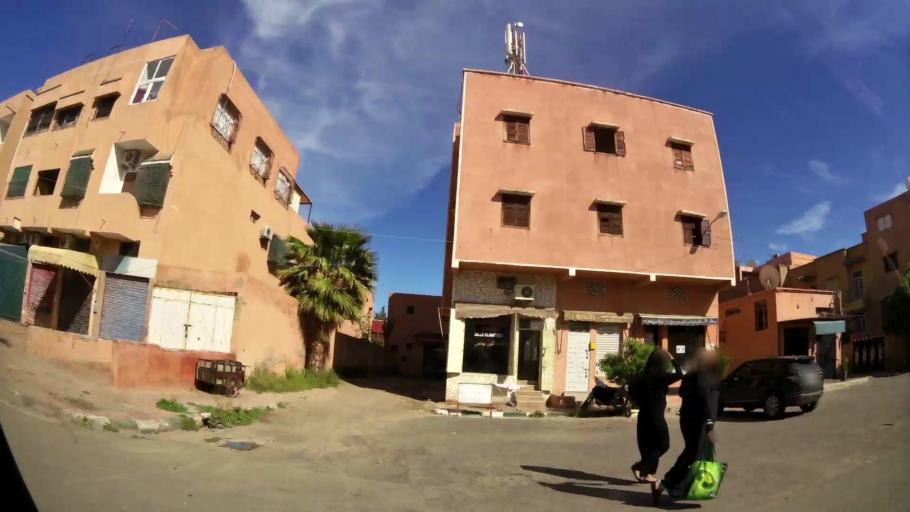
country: MA
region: Marrakech-Tensift-Al Haouz
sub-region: Marrakech
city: Marrakesh
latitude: 31.6548
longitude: -8.0116
